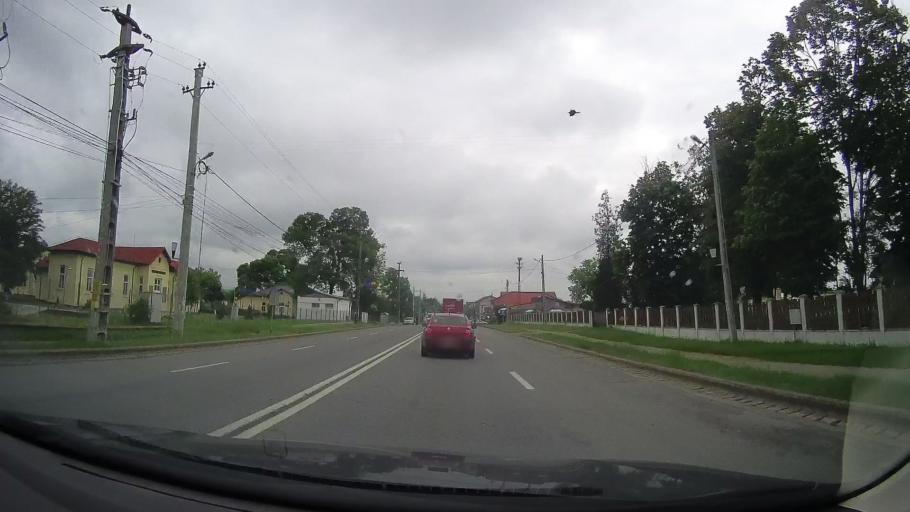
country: RO
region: Dolj
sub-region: Comuna Filiasi
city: Filiasi
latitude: 44.5581
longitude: 23.5022
